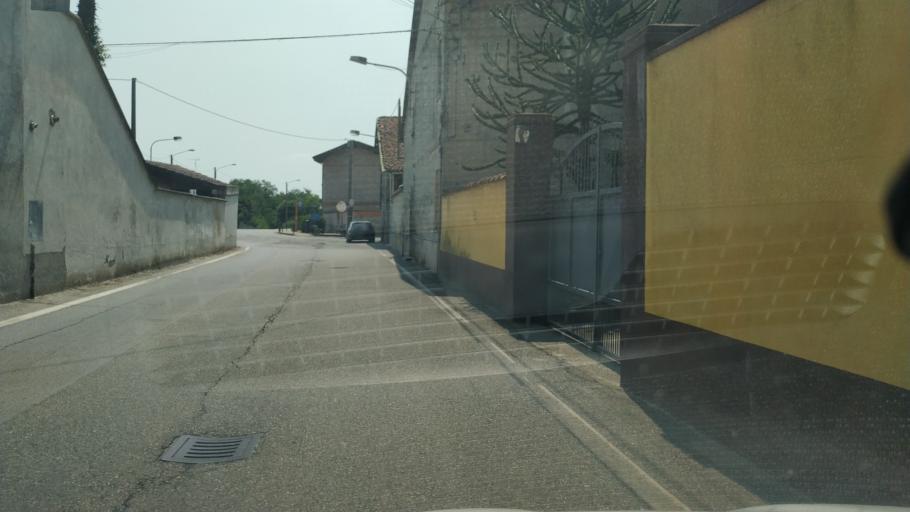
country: IT
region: Piedmont
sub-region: Provincia di Torino
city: Rondissone
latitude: 45.2442
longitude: 7.9683
